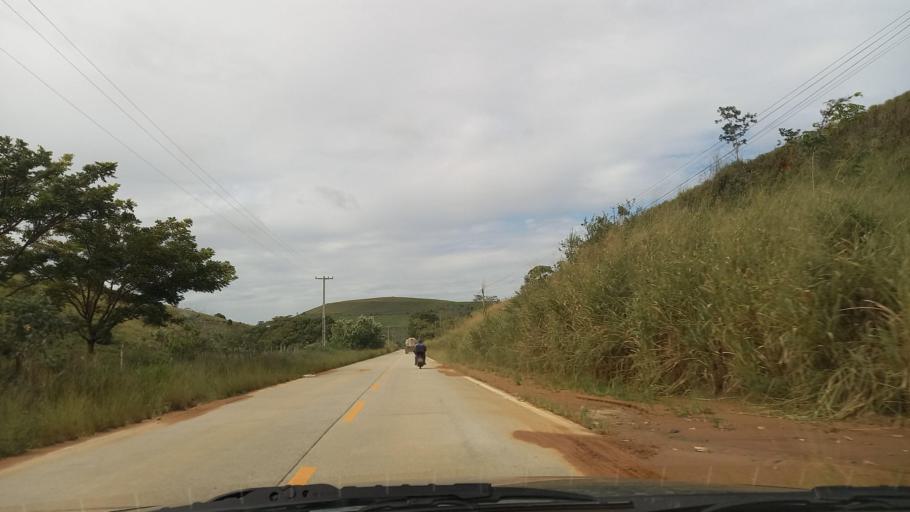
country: BR
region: Pernambuco
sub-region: Maraial
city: Maraial
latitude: -8.7528
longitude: -35.8388
